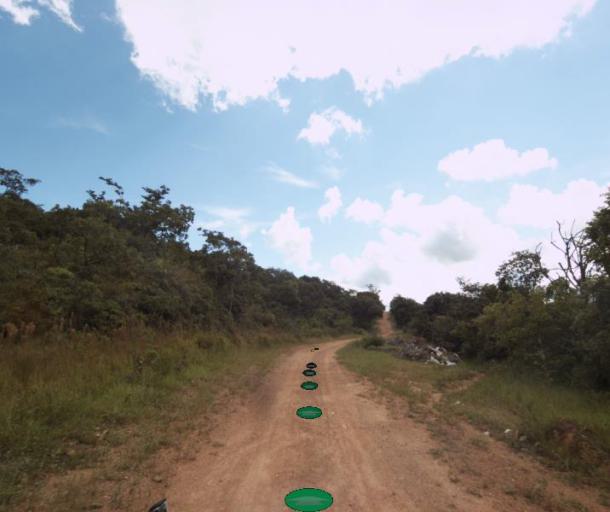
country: BR
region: Goias
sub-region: Pirenopolis
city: Pirenopolis
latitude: -15.7881
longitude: -48.9175
